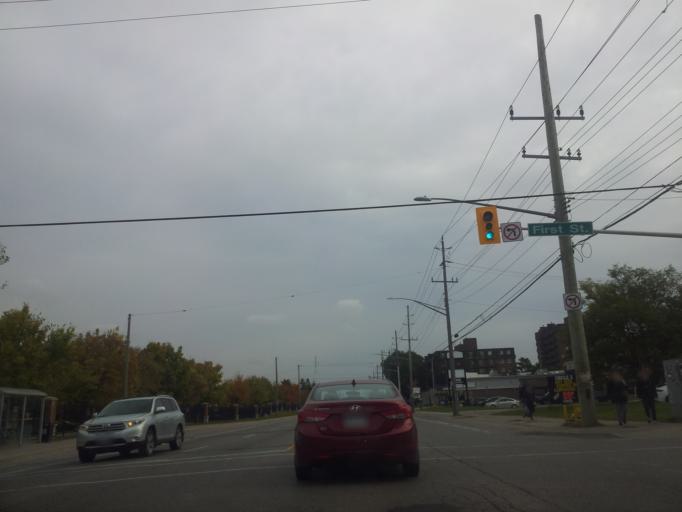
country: CA
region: Ontario
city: London
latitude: 43.0110
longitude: -81.2002
